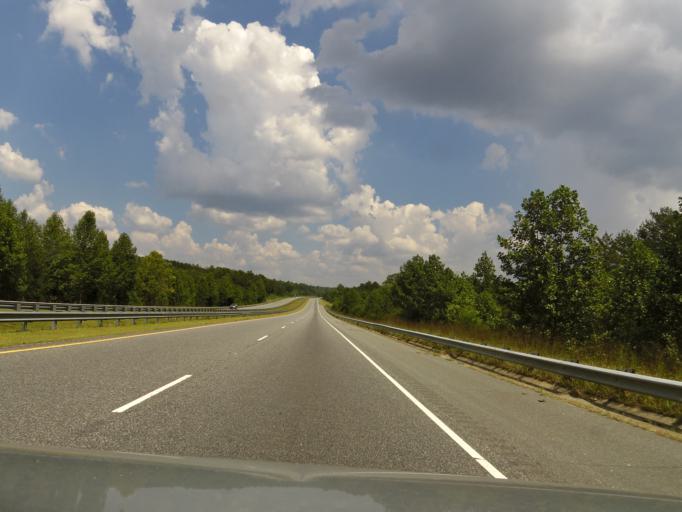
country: US
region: North Carolina
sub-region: Rutherford County
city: Spindale
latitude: 35.3015
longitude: -81.9638
